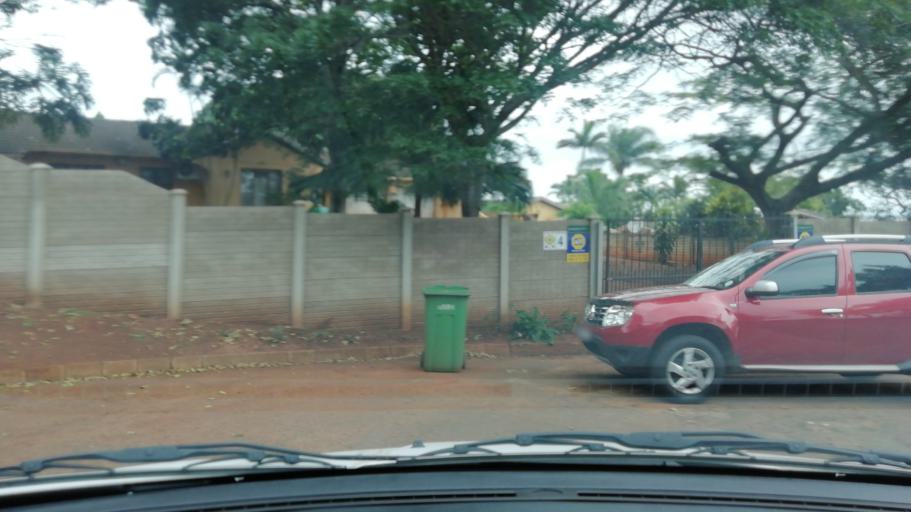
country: ZA
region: KwaZulu-Natal
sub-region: uThungulu District Municipality
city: Empangeni
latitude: -28.7634
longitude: 31.8898
